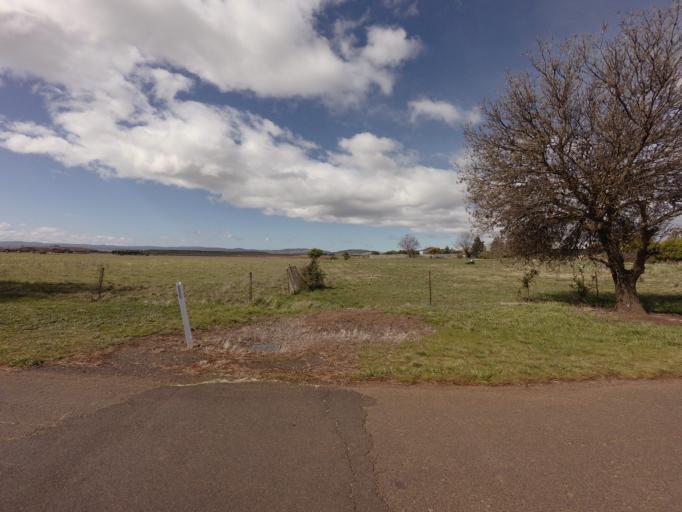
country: AU
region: Tasmania
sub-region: Northern Midlands
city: Evandale
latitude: -42.1355
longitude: 147.4278
